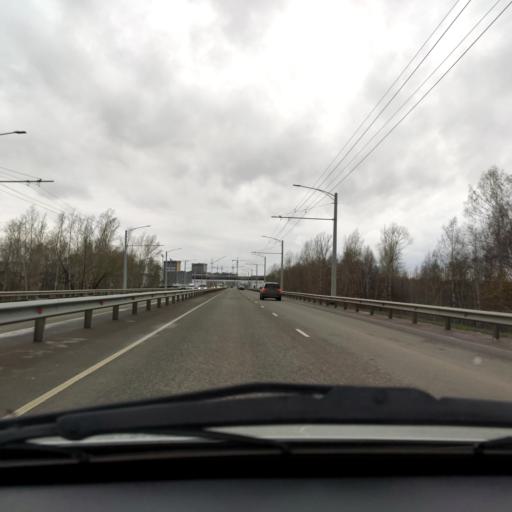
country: RU
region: Bashkortostan
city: Mikhaylovka
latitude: 54.7696
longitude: 55.9198
